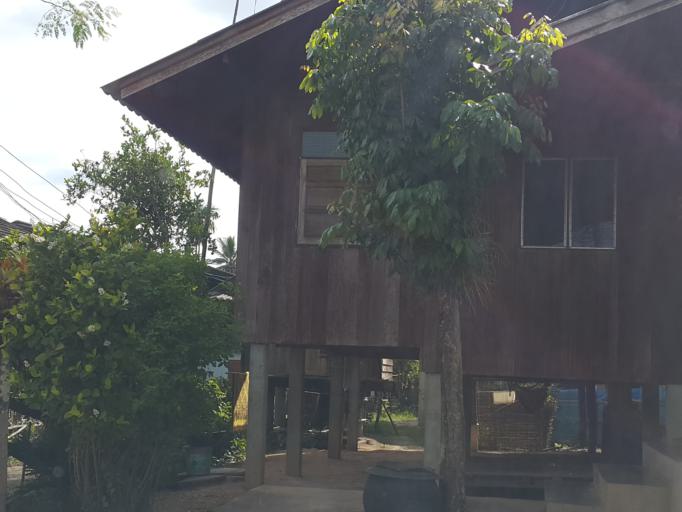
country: TH
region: Lampang
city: Chae Hom
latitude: 18.5626
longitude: 99.4481
